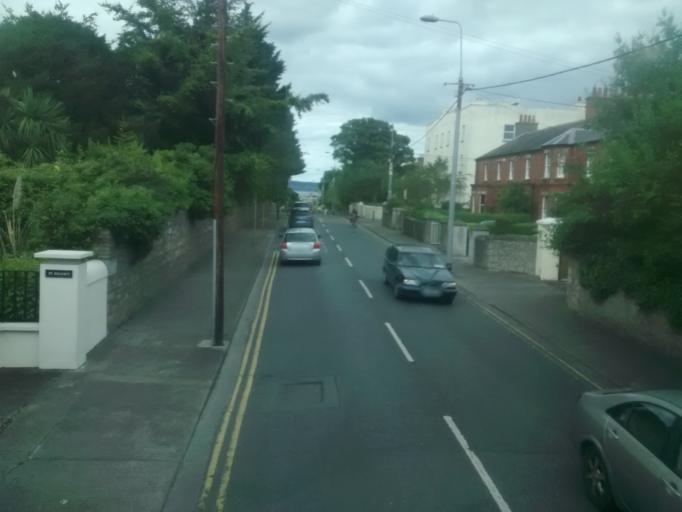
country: IE
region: Leinster
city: Monkstown
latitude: 53.2892
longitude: -6.1451
